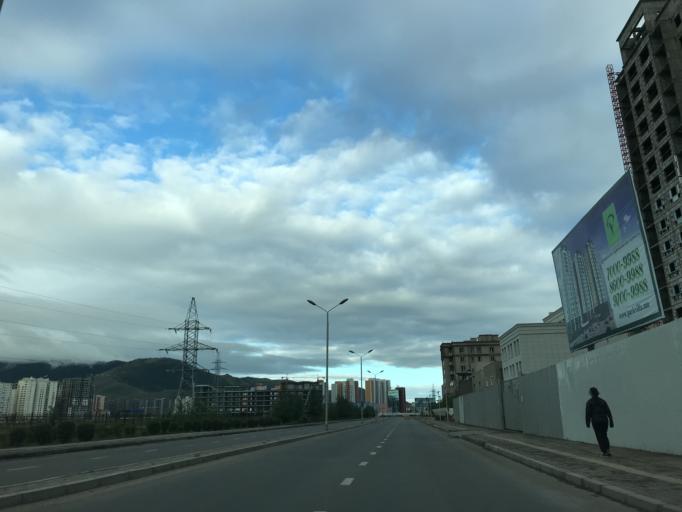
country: MN
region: Ulaanbaatar
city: Ulaanbaatar
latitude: 47.9014
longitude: 106.9365
